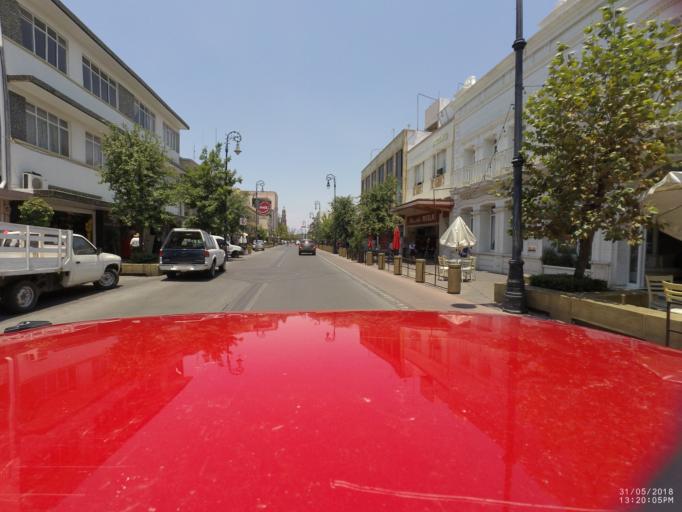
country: MX
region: Aguascalientes
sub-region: Aguascalientes
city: Aguascalientes
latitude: 21.8818
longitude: -102.2937
